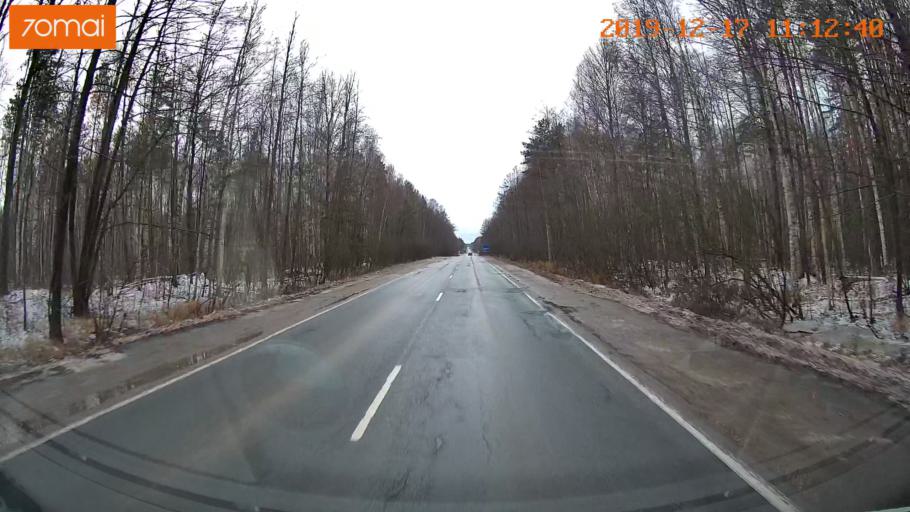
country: RU
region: Vladimir
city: Gus'-Khrustal'nyy
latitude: 55.5729
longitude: 40.6262
